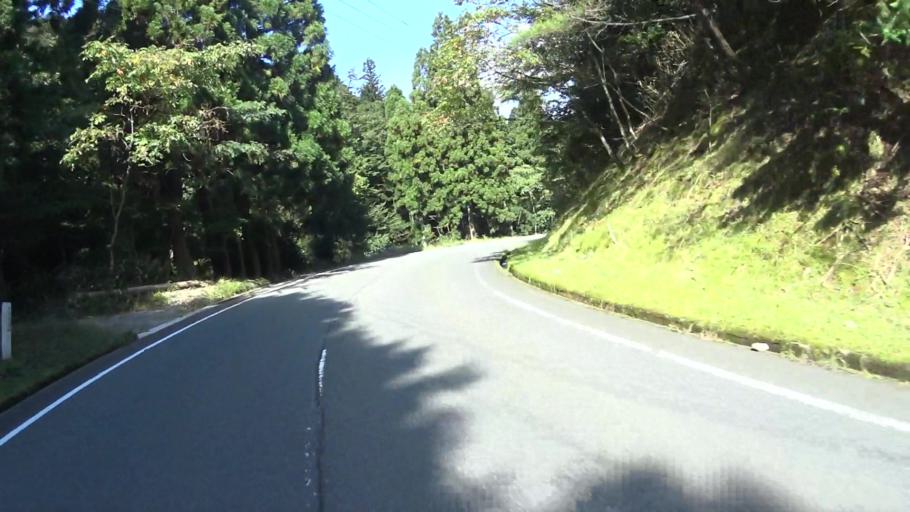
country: JP
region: Hyogo
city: Toyooka
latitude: 35.5370
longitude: 134.9769
